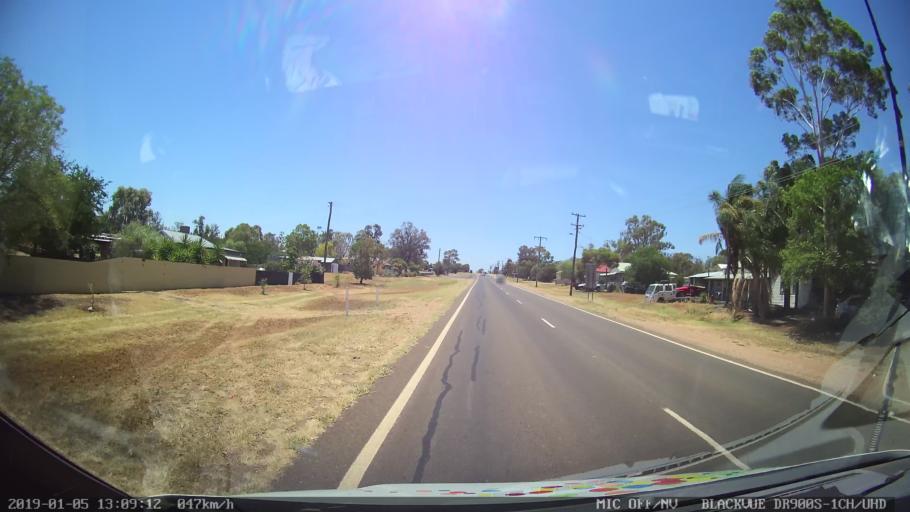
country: AU
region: New South Wales
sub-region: Gunnedah
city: Gunnedah
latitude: -31.0986
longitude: 149.9085
